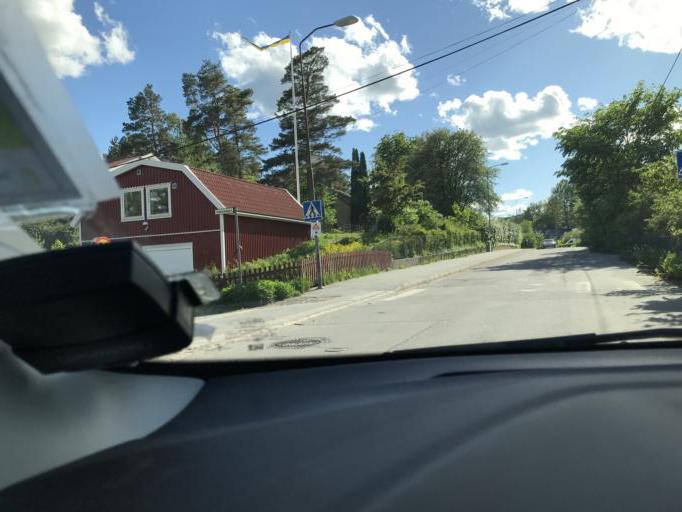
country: SE
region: Stockholm
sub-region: Botkyrka Kommun
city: Tumba
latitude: 59.1975
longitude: 17.8210
